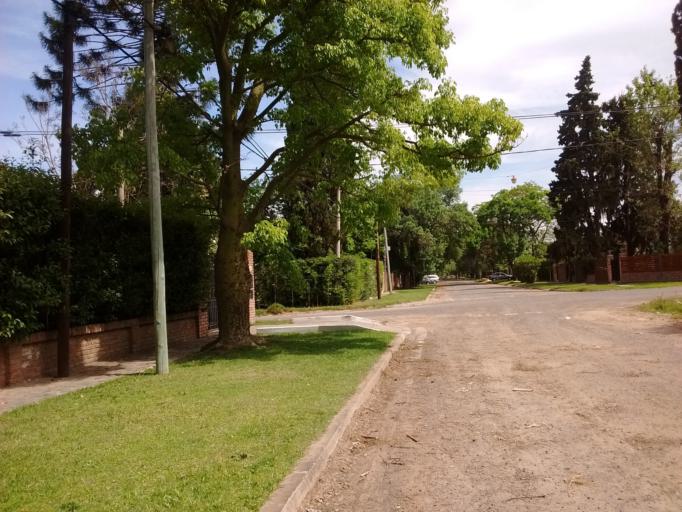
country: AR
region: Santa Fe
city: Funes
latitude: -32.9157
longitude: -60.8031
